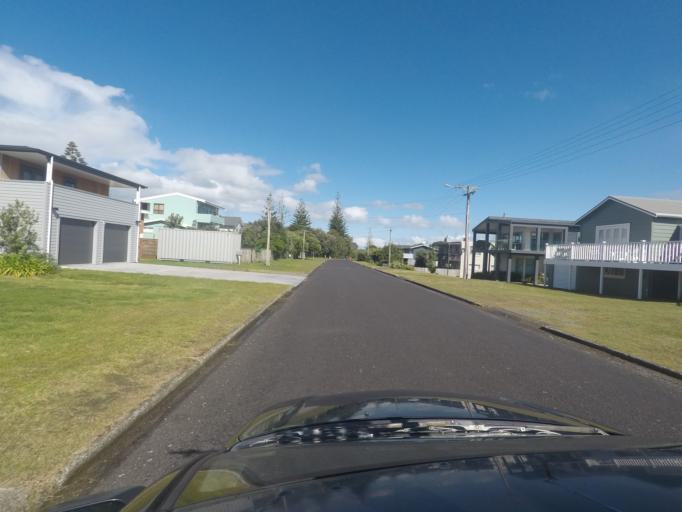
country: NZ
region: Bay of Plenty
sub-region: Western Bay of Plenty District
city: Waihi Beach
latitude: -37.4171
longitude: 175.9503
